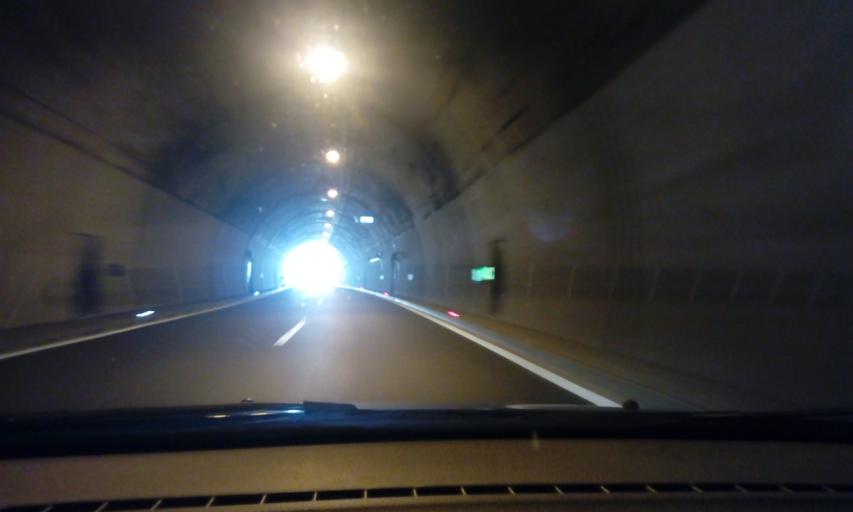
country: SI
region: Vipava
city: Vipava
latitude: 45.7993
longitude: 13.9816
